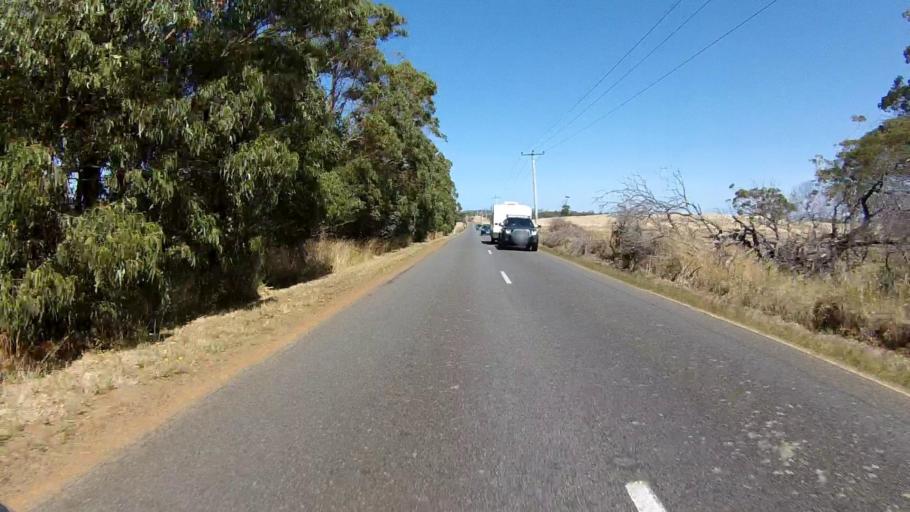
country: AU
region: Tasmania
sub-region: Sorell
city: Sorell
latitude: -42.2722
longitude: 148.0040
